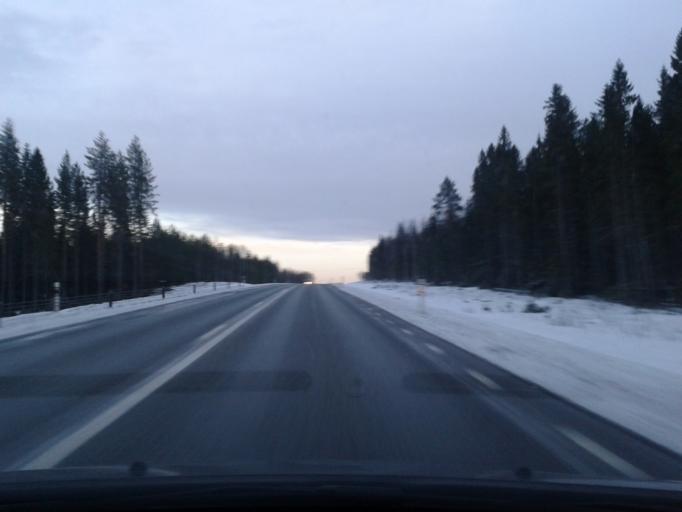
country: SE
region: Vaesternorrland
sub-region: Kramfors Kommun
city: Bollstabruk
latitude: 63.0610
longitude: 17.6006
